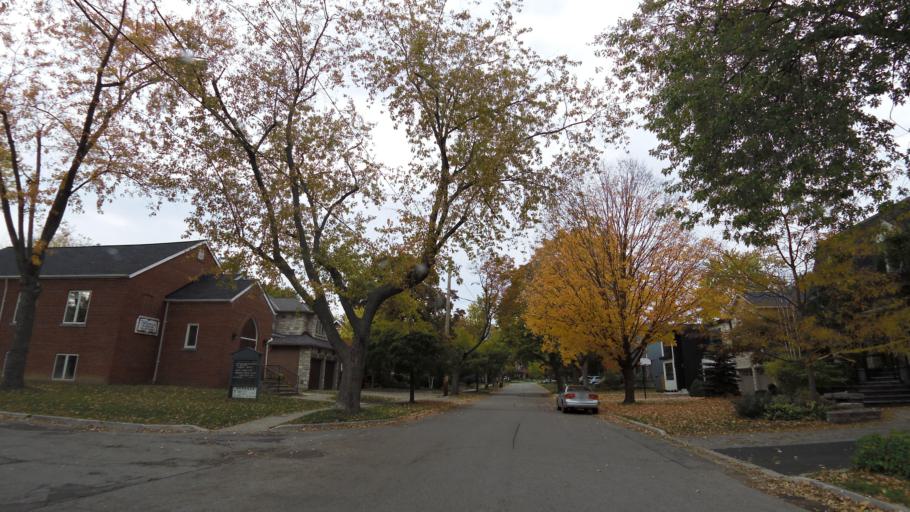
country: CA
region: Ontario
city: Etobicoke
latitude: 43.6461
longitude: -79.5334
